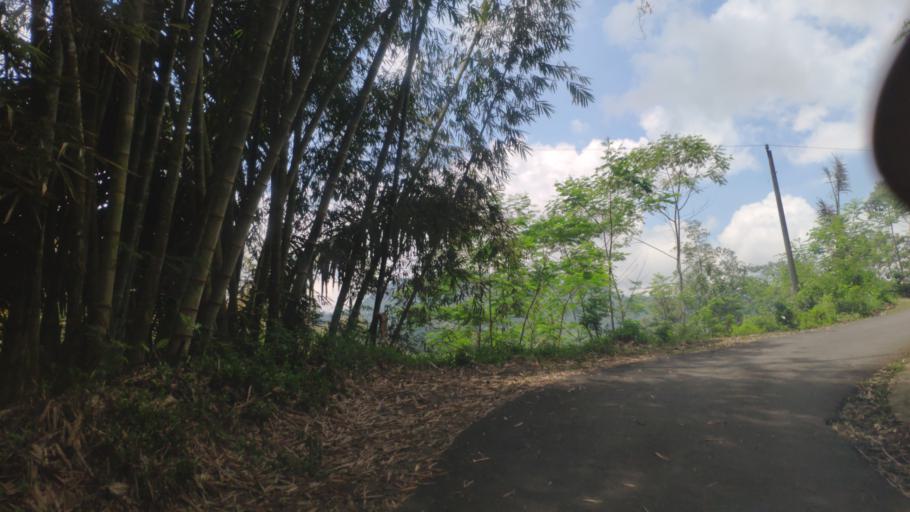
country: ID
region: Central Java
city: Wonosobo
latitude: -7.2632
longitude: 109.7291
